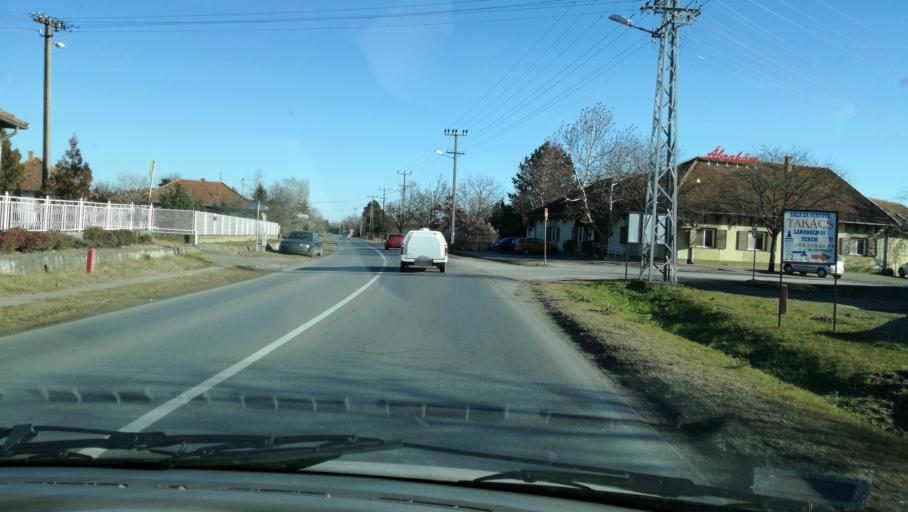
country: HU
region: Csongrad
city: Asotthalom
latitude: 46.1010
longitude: 19.7759
